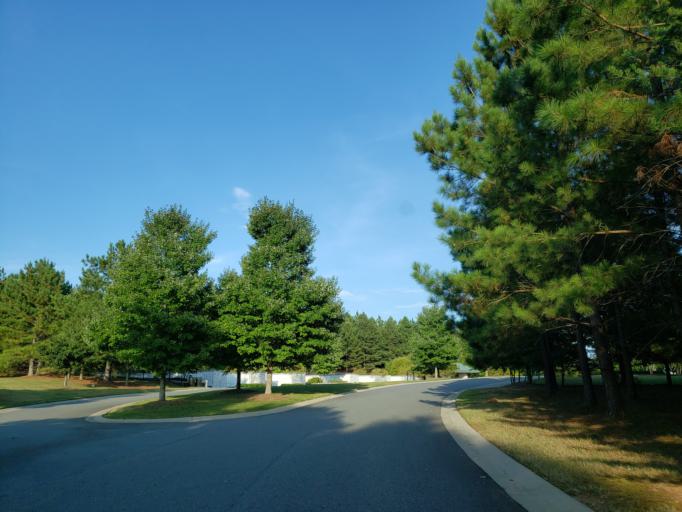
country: US
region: Georgia
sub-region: Cherokee County
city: Canton
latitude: 34.2353
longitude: -84.5815
